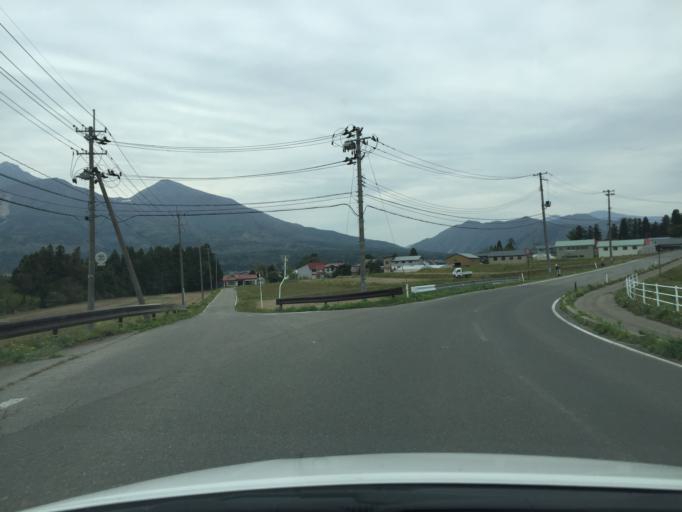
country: JP
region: Fukushima
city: Inawashiro
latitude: 37.5614
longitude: 140.1339
